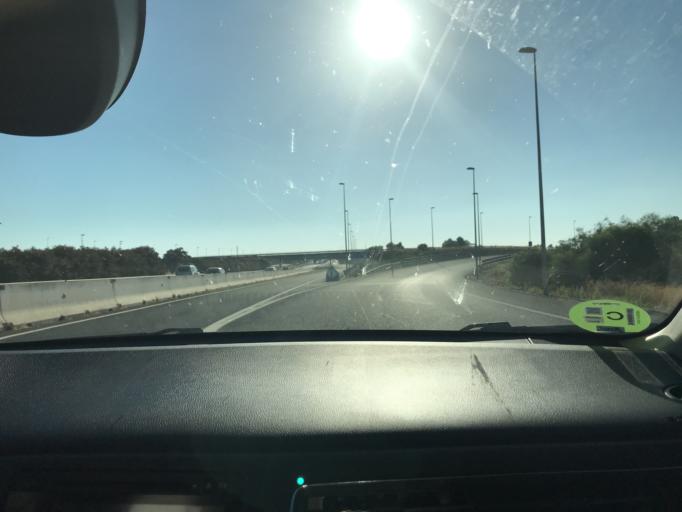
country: ES
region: Andalusia
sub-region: Provincia de Sevilla
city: Alcala de Guadaira
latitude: 37.4321
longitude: -5.8366
